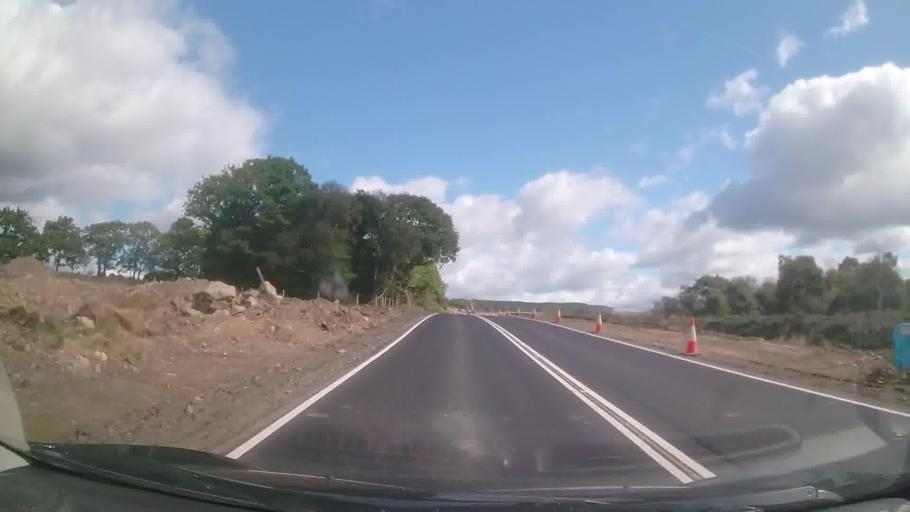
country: GB
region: Wales
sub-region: Rhondda Cynon Taf
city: Hirwaun
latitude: 51.7477
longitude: -3.4759
